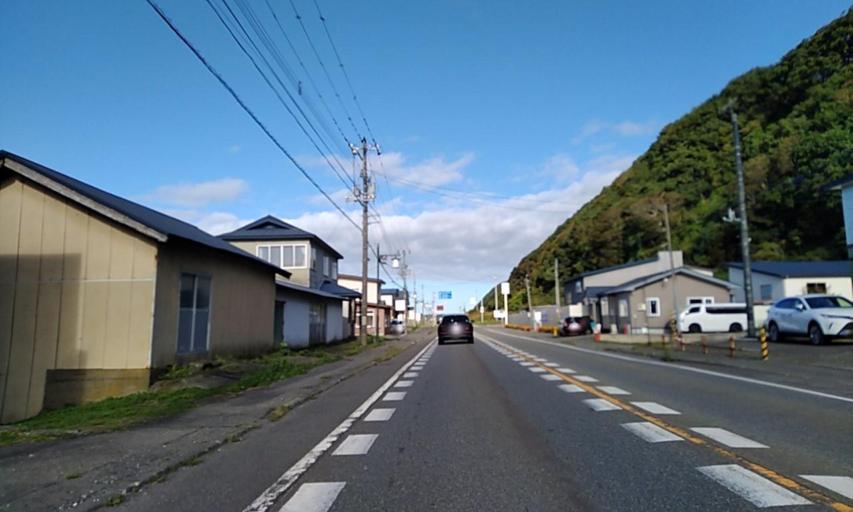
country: JP
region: Hokkaido
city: Shizunai-furukawacho
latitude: 42.2547
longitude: 142.5367
